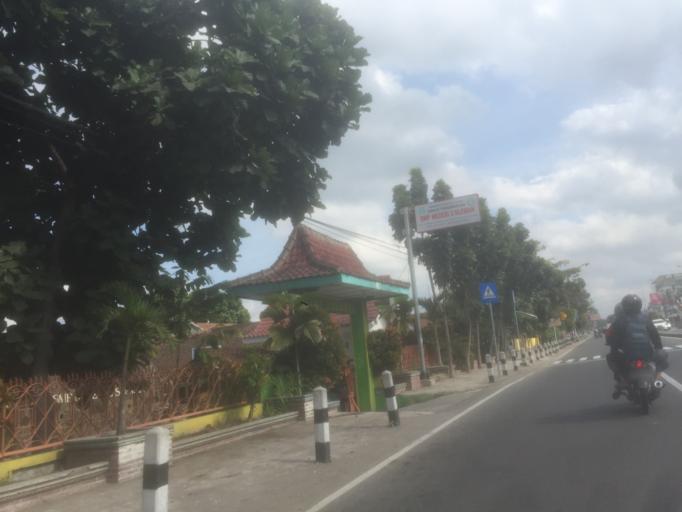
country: ID
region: Daerah Istimewa Yogyakarta
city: Sleman
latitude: -7.6904
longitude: 110.3432
